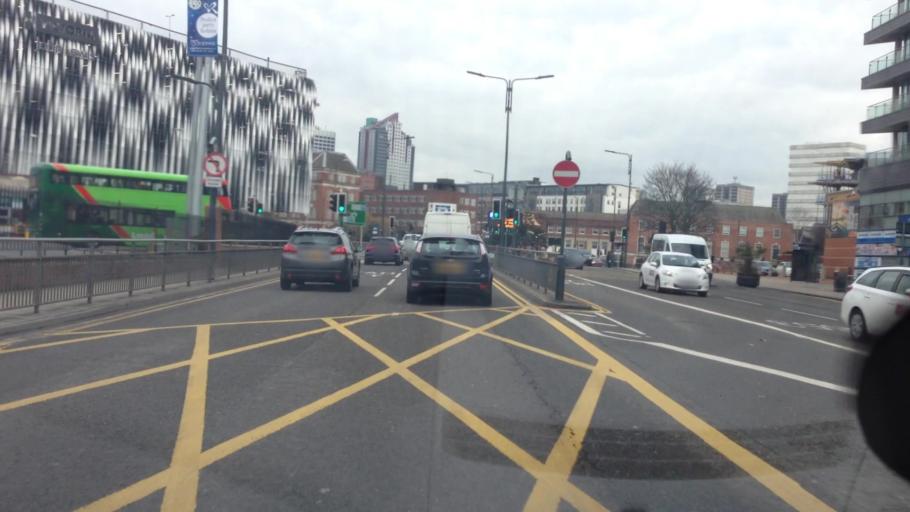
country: GB
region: England
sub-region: City and Borough of Leeds
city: Leeds
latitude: 53.7972
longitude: -1.5347
